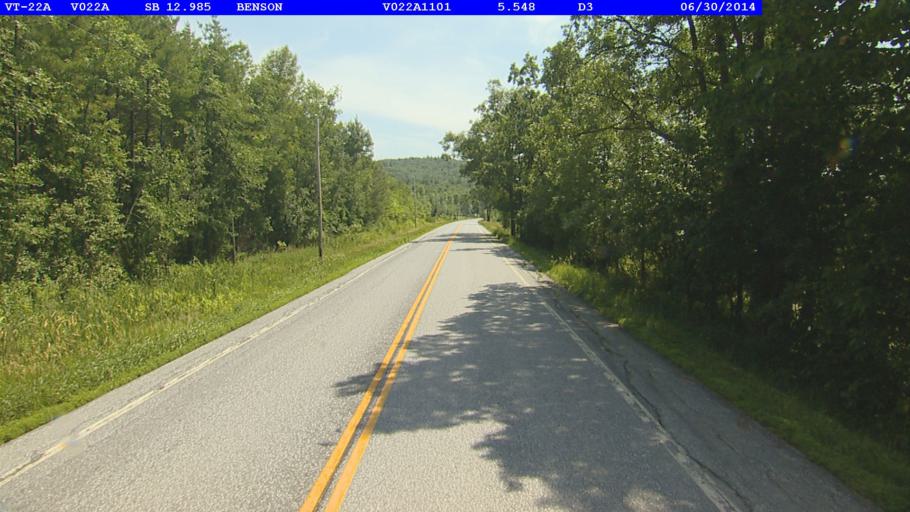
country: US
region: New York
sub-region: Essex County
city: Ticonderoga
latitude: 43.7473
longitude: -73.3079
